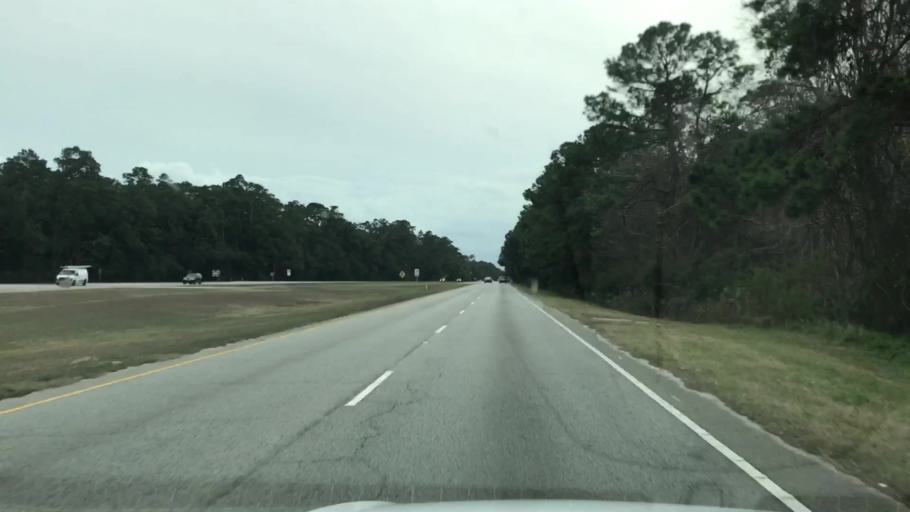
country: US
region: South Carolina
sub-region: Georgetown County
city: Murrells Inlet
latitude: 33.5294
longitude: -79.0623
